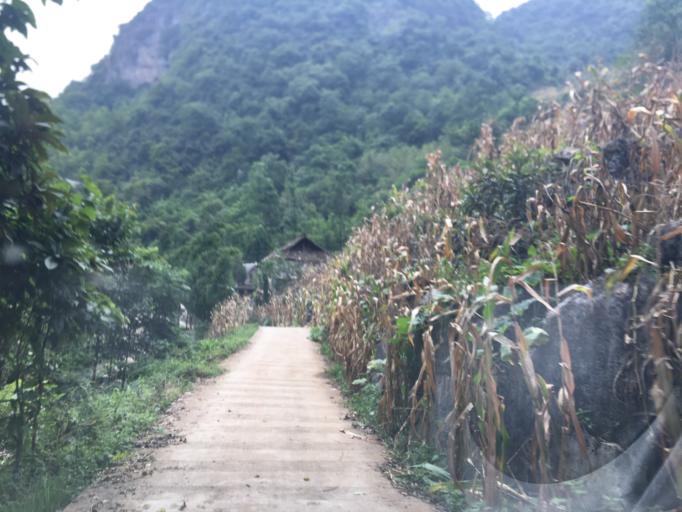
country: CN
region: Guangxi Zhuangzu Zizhiqu
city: Xinzhou
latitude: 25.2294
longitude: 105.6419
